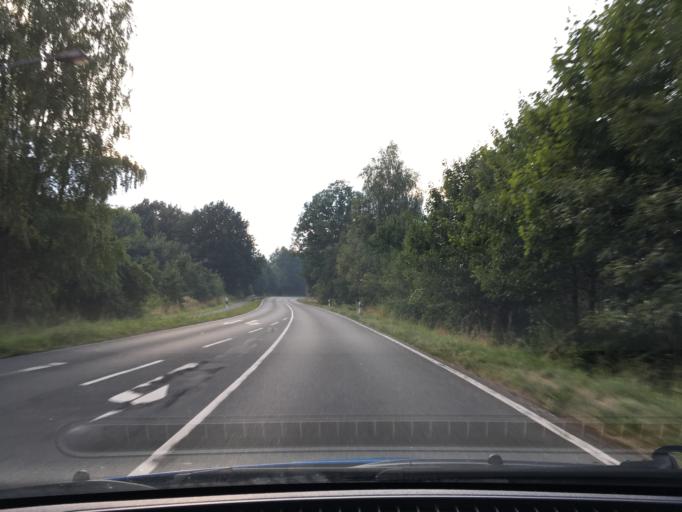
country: DE
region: Lower Saxony
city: Hermannsburg
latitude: 52.7551
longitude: 10.0494
